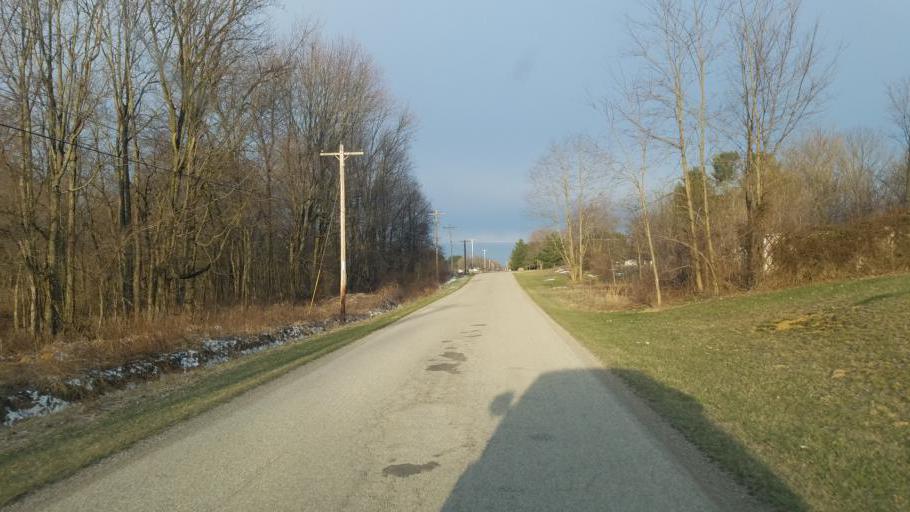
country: US
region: Ohio
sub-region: Knox County
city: Centerburg
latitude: 40.3908
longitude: -82.7517
